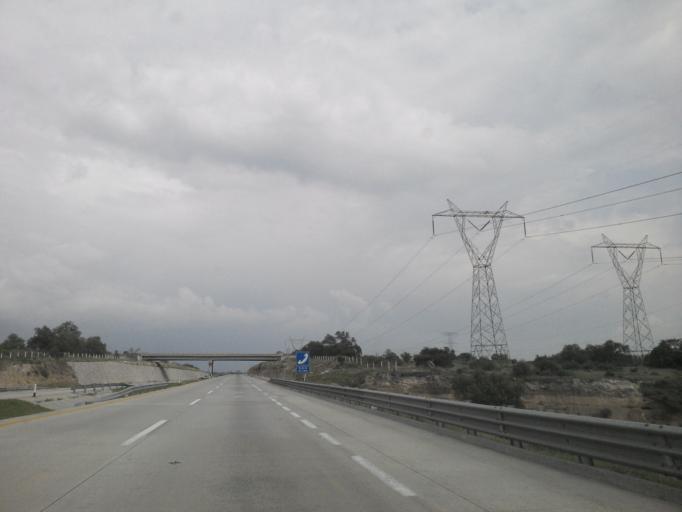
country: MX
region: Mexico
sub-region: Apaxco
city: Colonia Juarez
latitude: 20.0006
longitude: -99.1403
